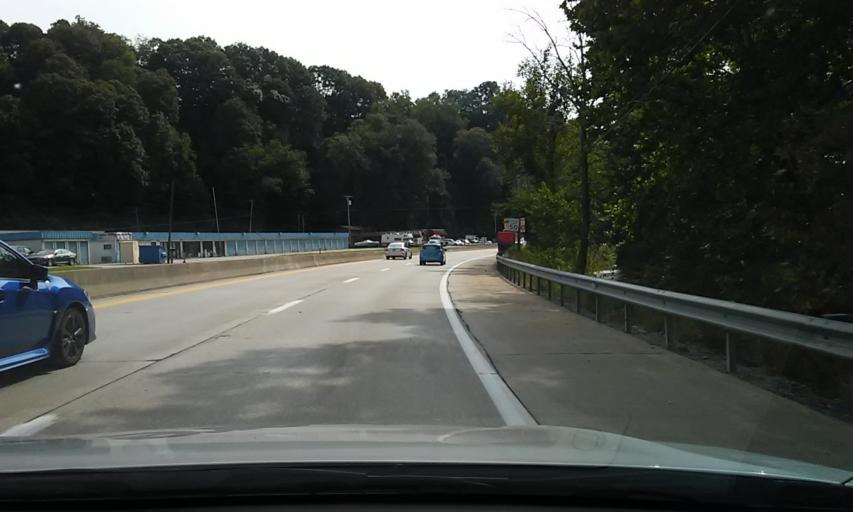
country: US
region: Pennsylvania
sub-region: Fayette County
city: Connellsville
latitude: 40.0486
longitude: -79.5653
